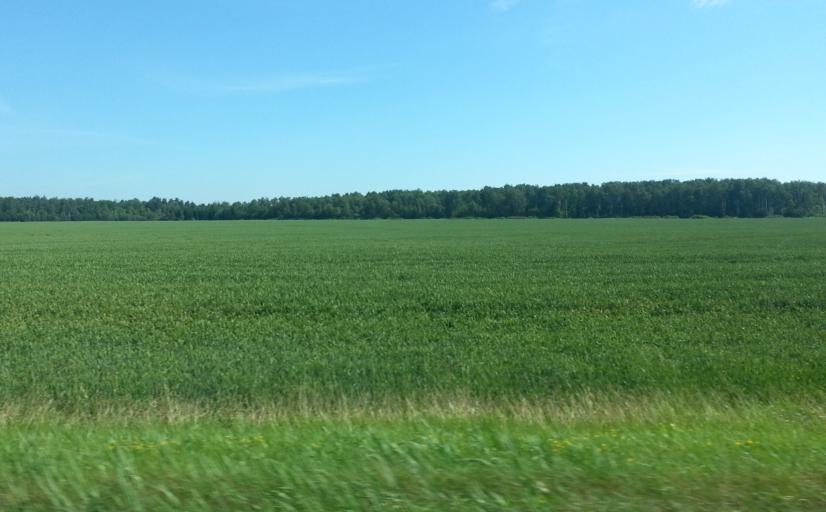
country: LT
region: Panevezys
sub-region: Panevezys City
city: Panevezys
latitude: 55.6858
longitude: 24.2855
